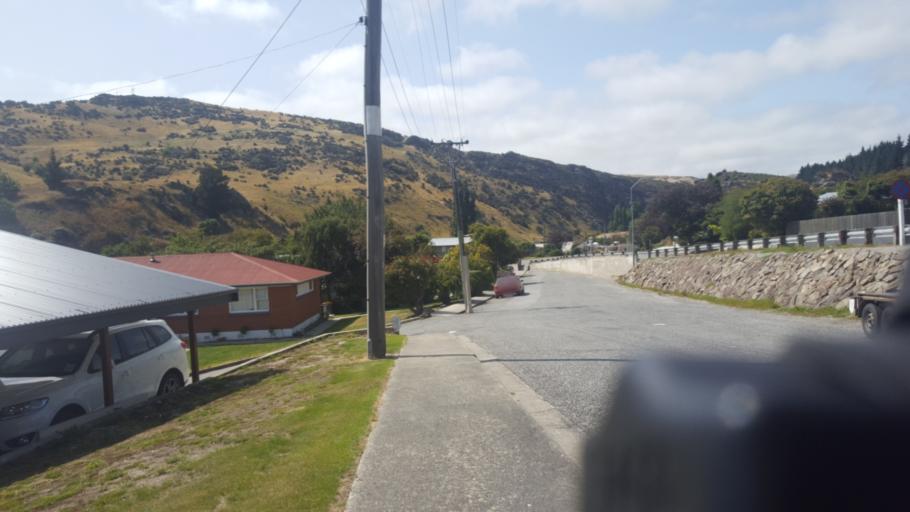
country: NZ
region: Otago
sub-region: Queenstown-Lakes District
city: Kingston
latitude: -45.5423
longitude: 169.3183
